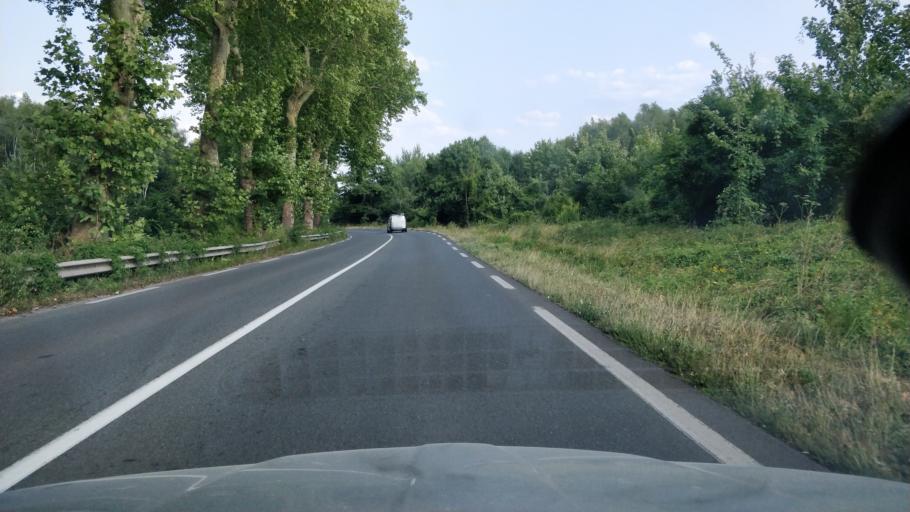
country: FR
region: Ile-de-France
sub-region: Departement de Seine-et-Marne
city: Vaires-sur-Marne
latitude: 48.8817
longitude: 2.6560
